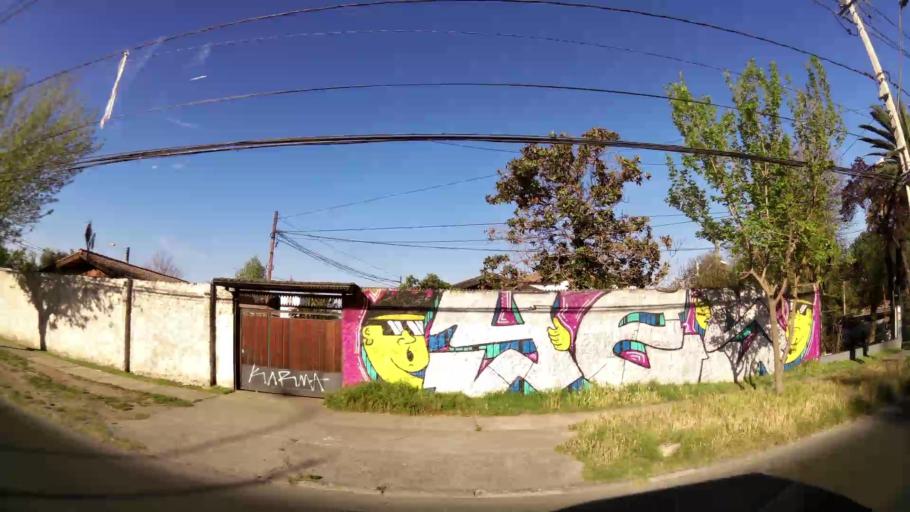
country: CL
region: Santiago Metropolitan
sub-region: Provincia de Santiago
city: Villa Presidente Frei, Nunoa, Santiago, Chile
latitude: -33.4427
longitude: -70.5692
